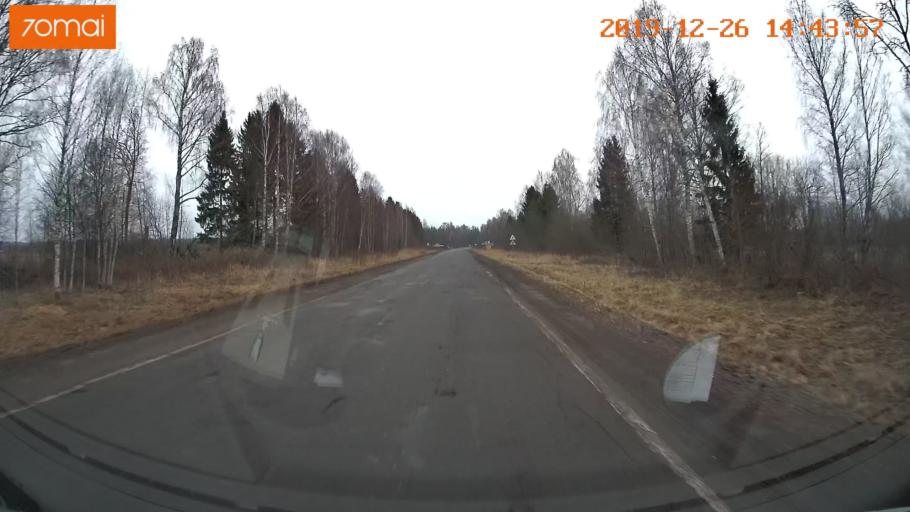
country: RU
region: Jaroslavl
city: Poshekhon'ye
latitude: 58.3522
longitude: 39.0458
